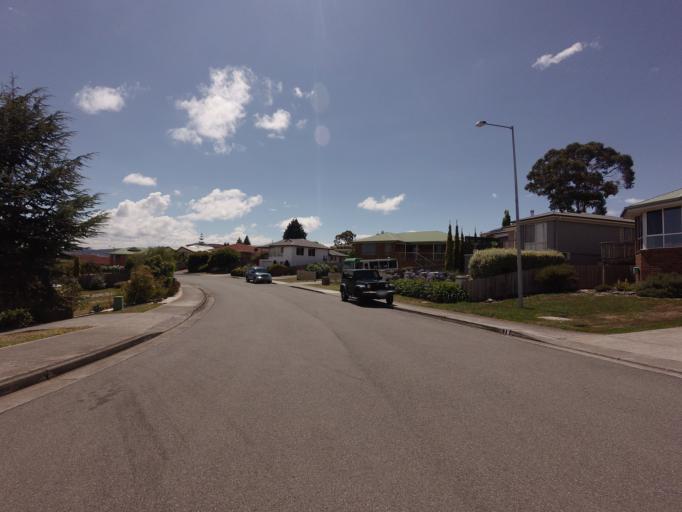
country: AU
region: Tasmania
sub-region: Clarence
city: Howrah
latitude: -42.9194
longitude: 147.4128
